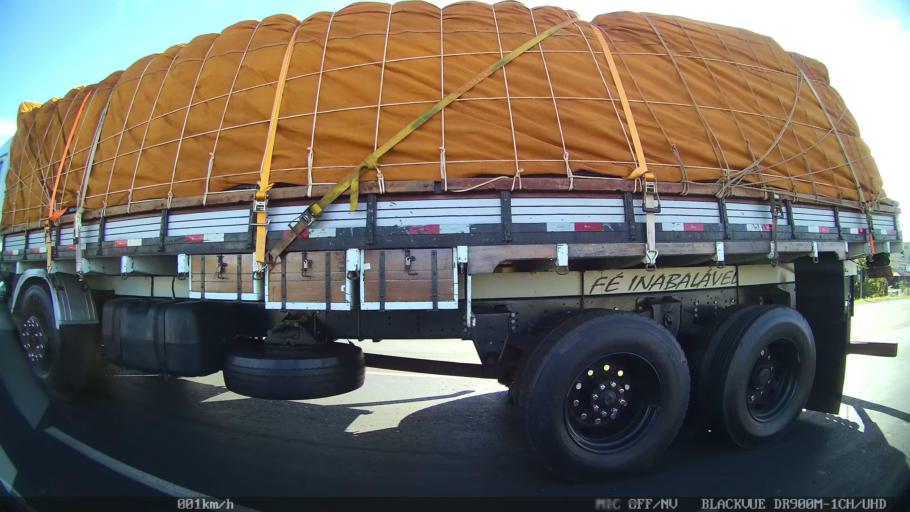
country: BR
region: Sao Paulo
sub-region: Sao Jose Do Rio Preto
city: Sao Jose do Rio Preto
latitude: -20.8004
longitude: -49.3560
